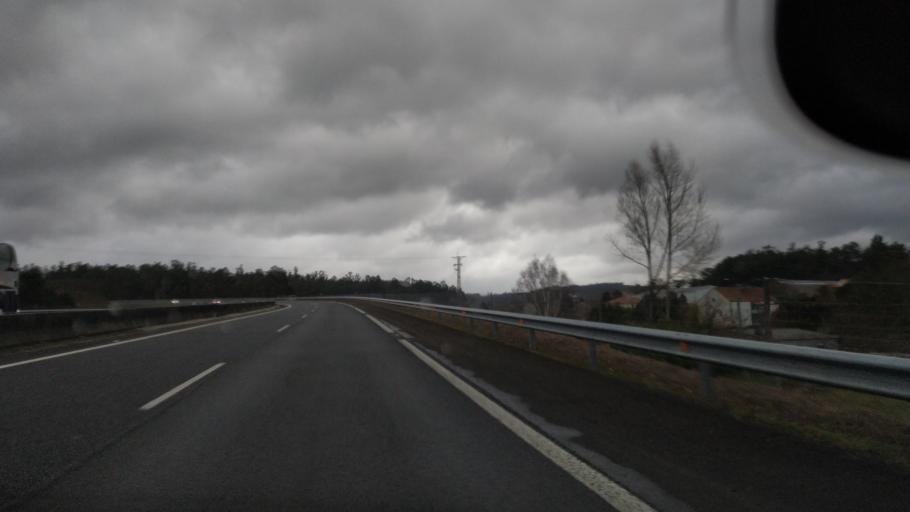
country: ES
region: Galicia
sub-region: Provincia da Coruna
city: Vedra
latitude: 42.8166
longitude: -8.4870
